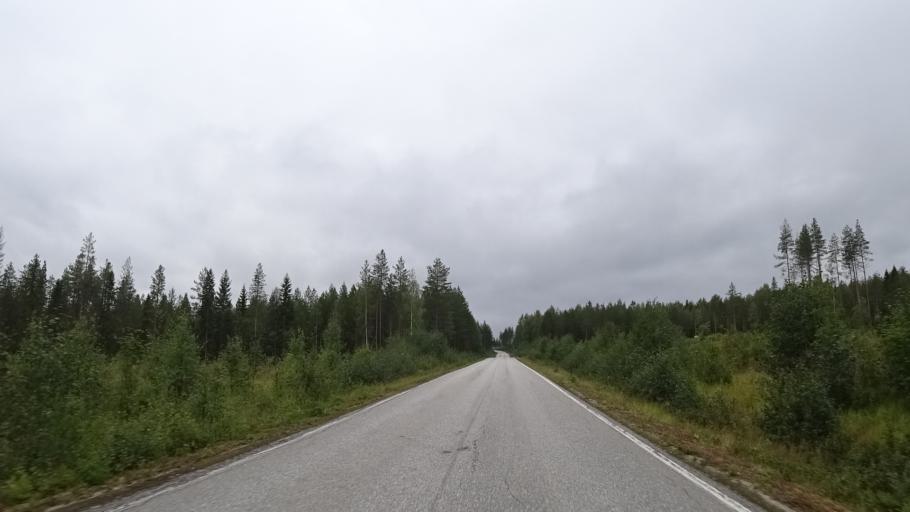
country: FI
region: North Karelia
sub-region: Pielisen Karjala
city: Lieksa
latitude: 63.3713
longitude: 30.2984
